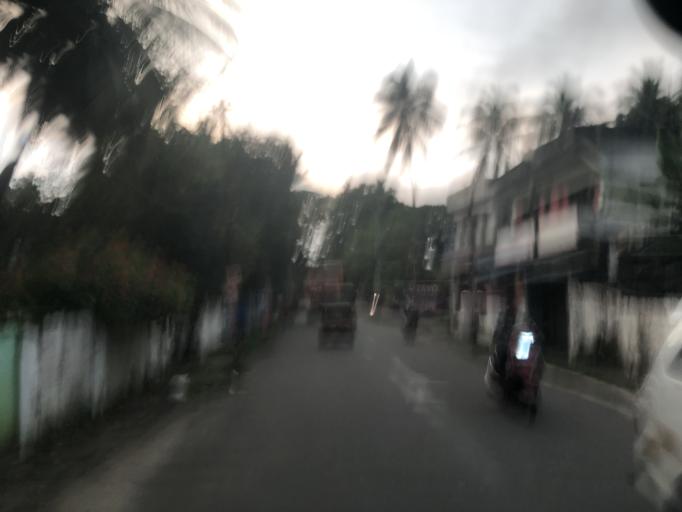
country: IN
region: Kerala
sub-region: Ernakulam
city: Cochin
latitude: 9.9523
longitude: 76.2460
